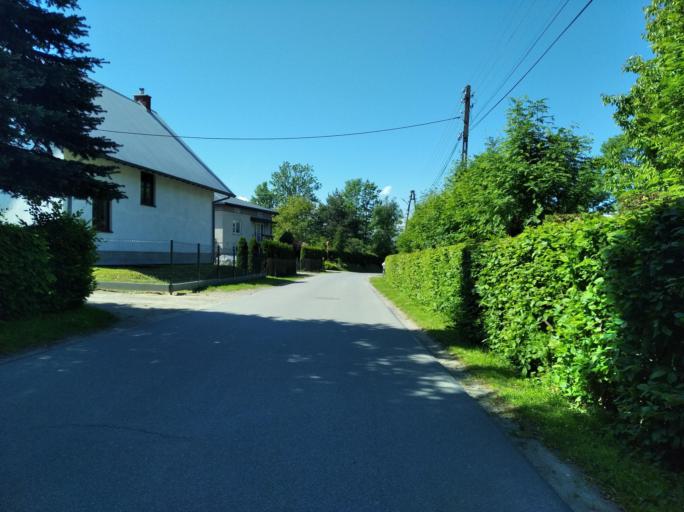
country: PL
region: Subcarpathian Voivodeship
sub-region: Powiat krosnienski
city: Odrzykon
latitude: 49.7368
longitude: 21.7332
